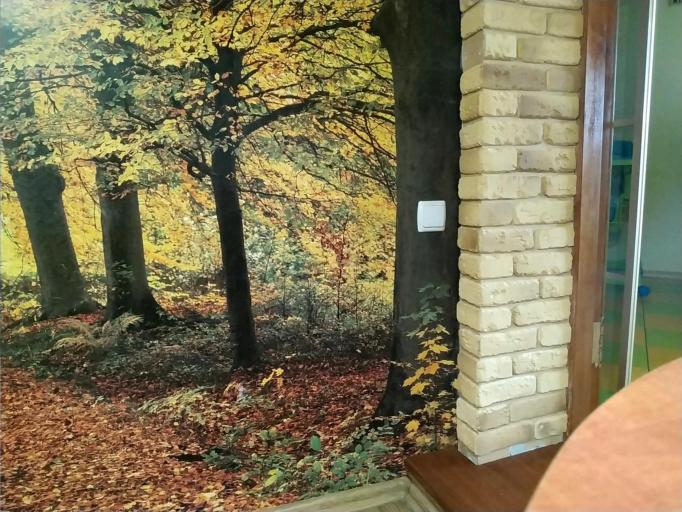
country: RU
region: Smolensk
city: Dorogobuzh
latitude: 54.9123
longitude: 33.3287
